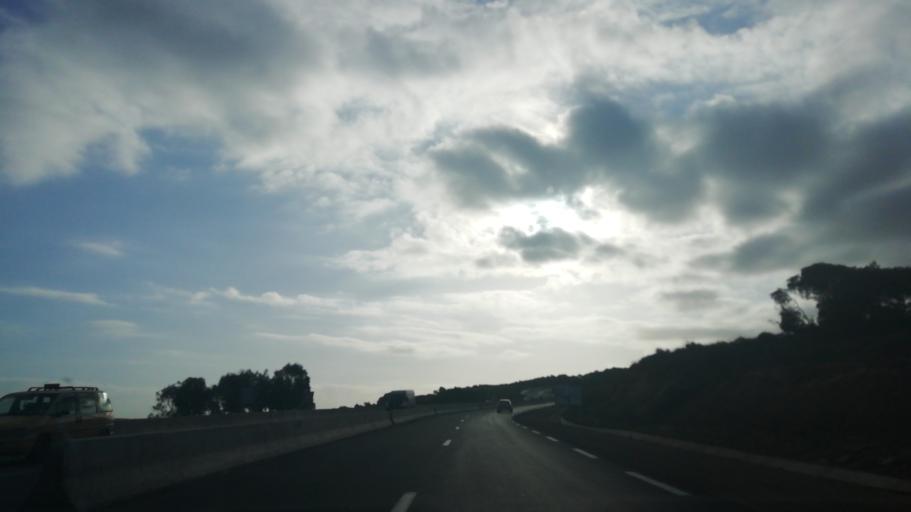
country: DZ
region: Mostaganem
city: Mostaganem
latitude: 36.1114
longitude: 0.2581
